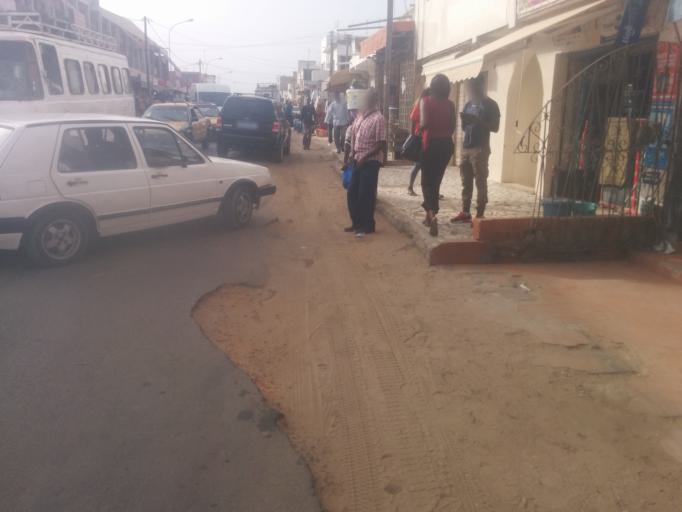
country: SN
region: Dakar
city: Grand Dakar
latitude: 14.7585
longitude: -17.4478
